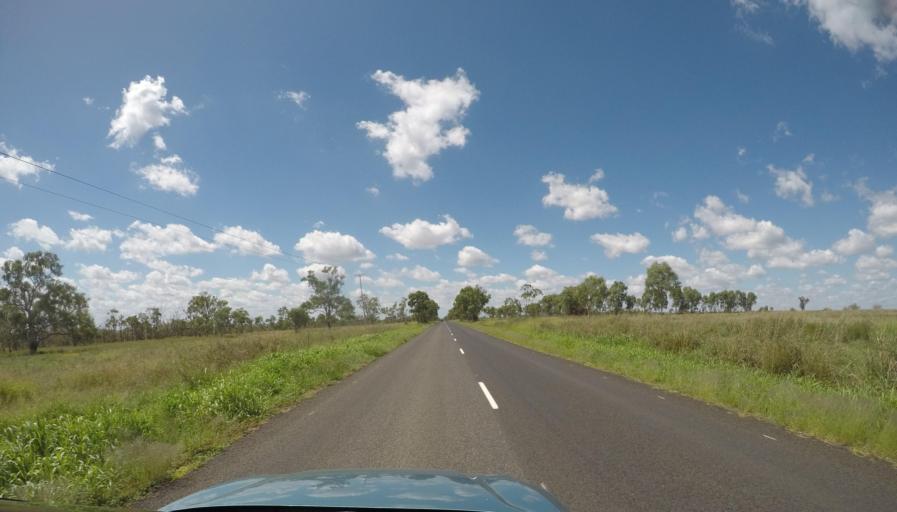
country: AU
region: Queensland
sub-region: Toowoomba
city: Oakey
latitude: -27.5293
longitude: 151.5948
